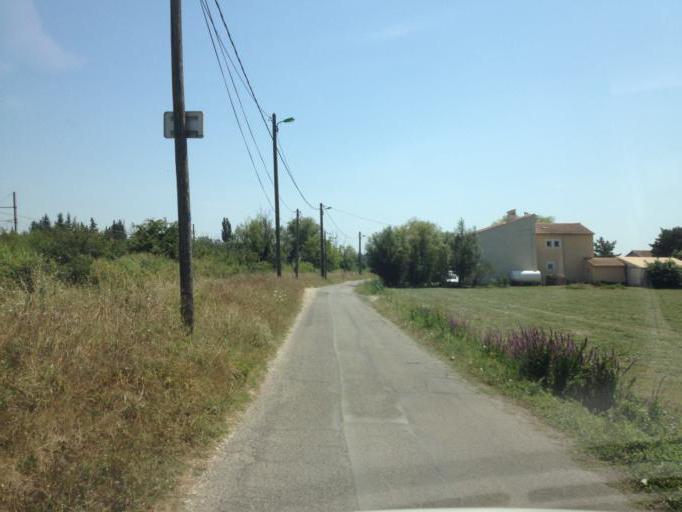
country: FR
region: Provence-Alpes-Cote d'Azur
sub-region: Departement du Vaucluse
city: Bedarrides
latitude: 44.0495
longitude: 4.8937
